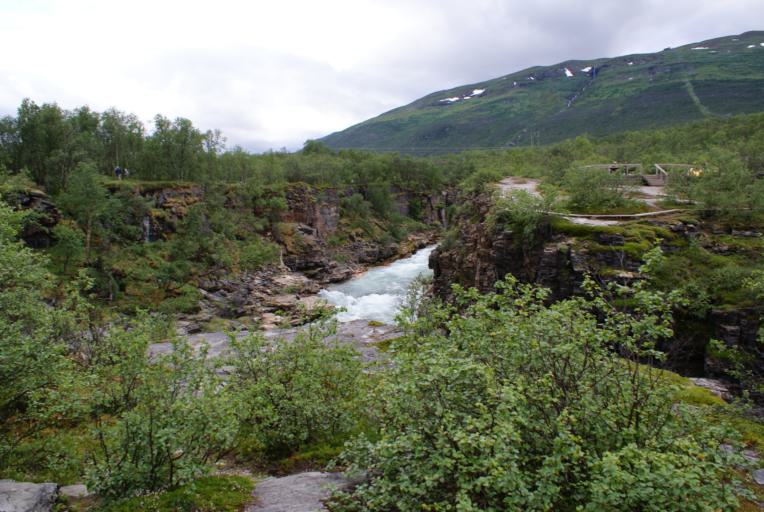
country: NO
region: Troms
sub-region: Bardu
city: Setermoen
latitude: 68.3604
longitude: 18.7824
